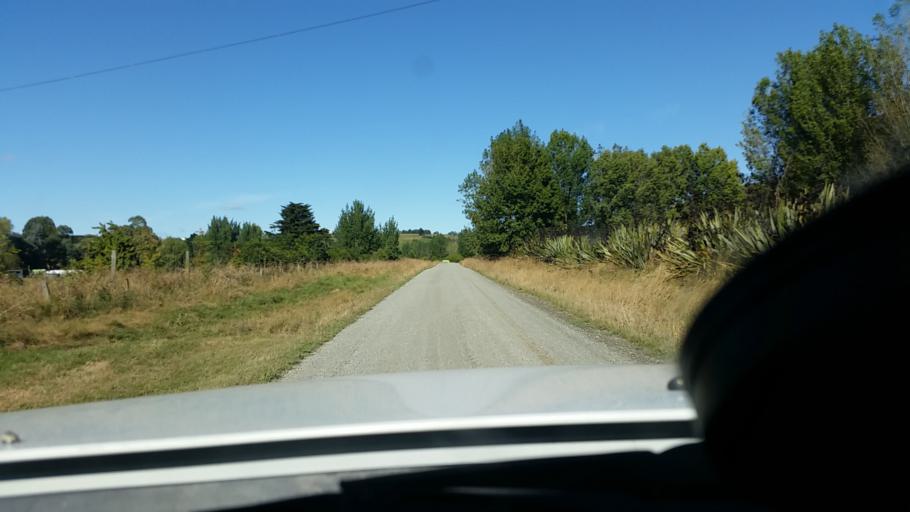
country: NZ
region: Canterbury
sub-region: Timaru District
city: Pleasant Point
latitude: -44.3407
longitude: 171.1653
